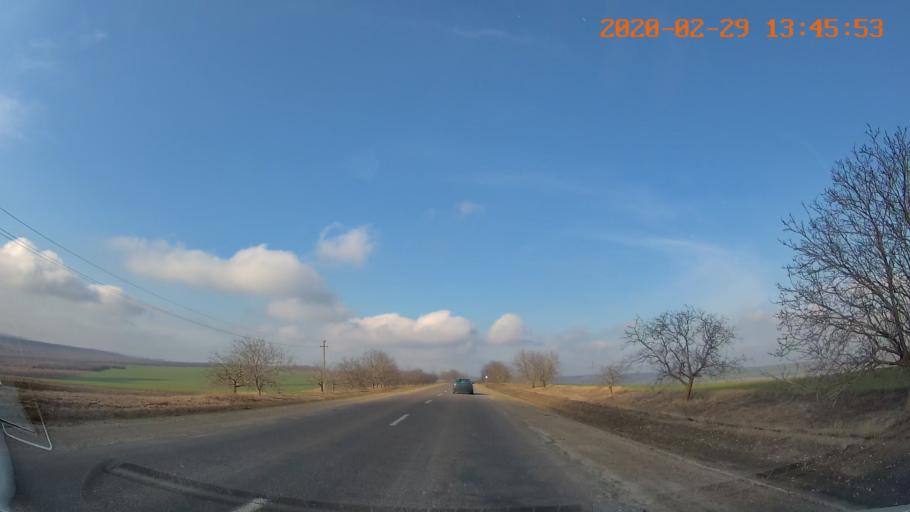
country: MD
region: Floresti
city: Leninskiy
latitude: 47.8521
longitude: 28.5117
